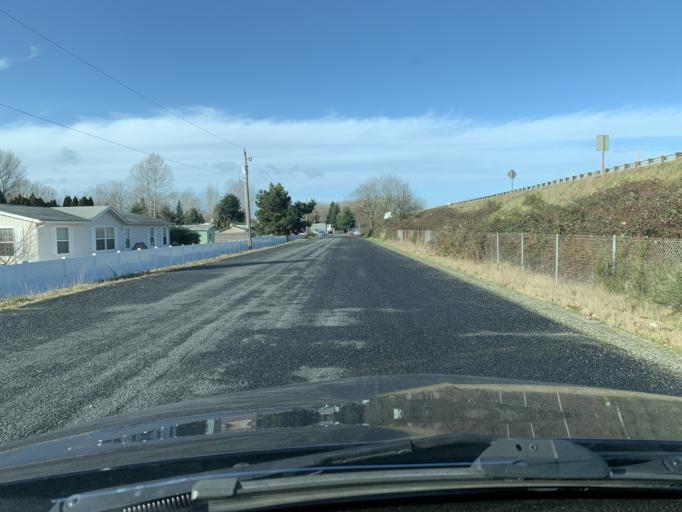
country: US
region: Washington
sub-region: Pierce County
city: North Puyallup
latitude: 47.2031
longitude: -122.2870
